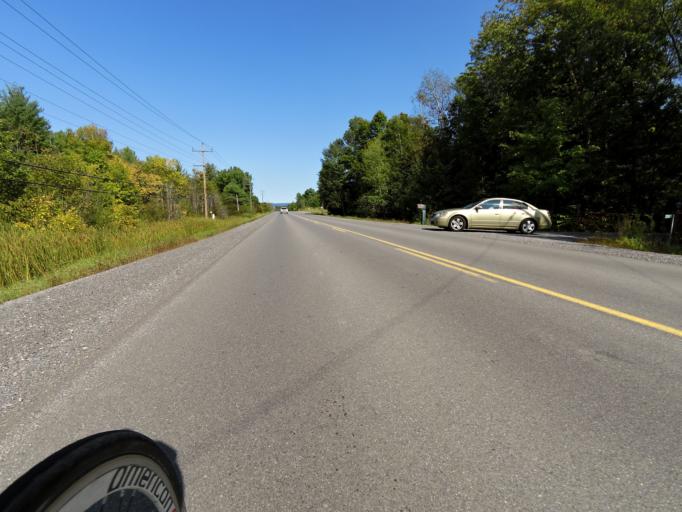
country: CA
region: Ontario
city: Arnprior
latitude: 45.4287
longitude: -76.1286
